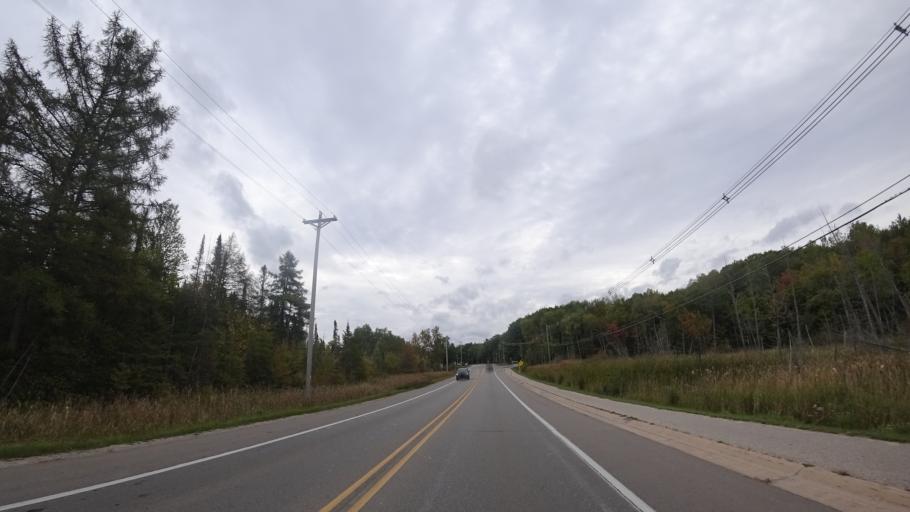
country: US
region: Michigan
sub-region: Emmet County
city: Petoskey
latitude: 45.4166
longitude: -84.9045
